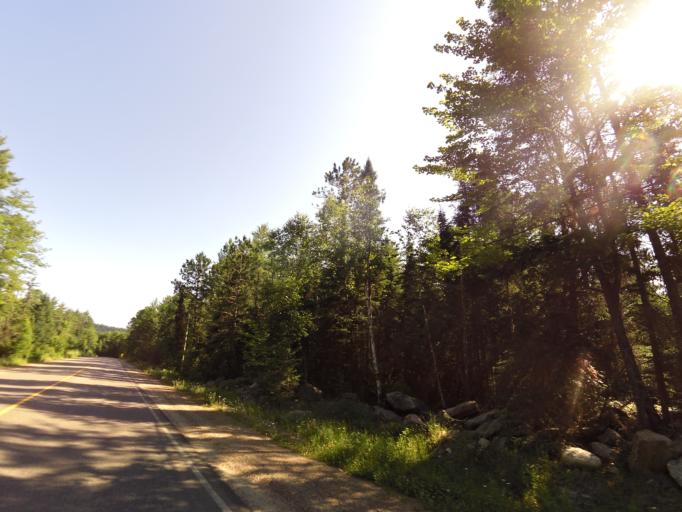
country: CA
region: Ontario
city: Deep River
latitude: 46.1875
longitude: -77.6809
